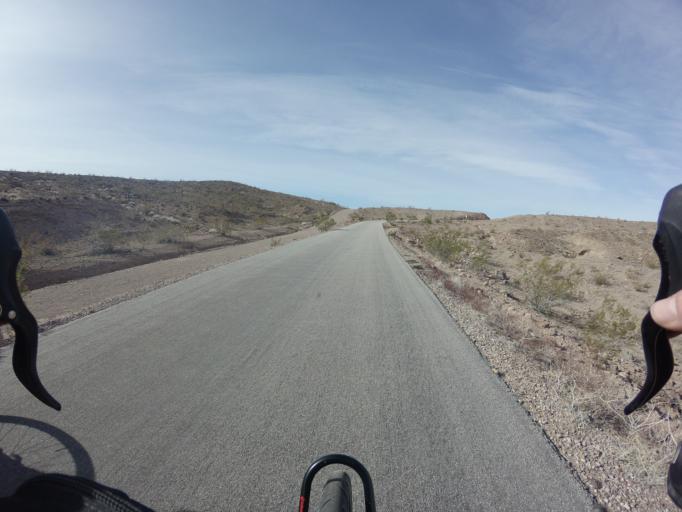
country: US
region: Nevada
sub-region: Clark County
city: Henderson
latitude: 36.1115
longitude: -114.8739
